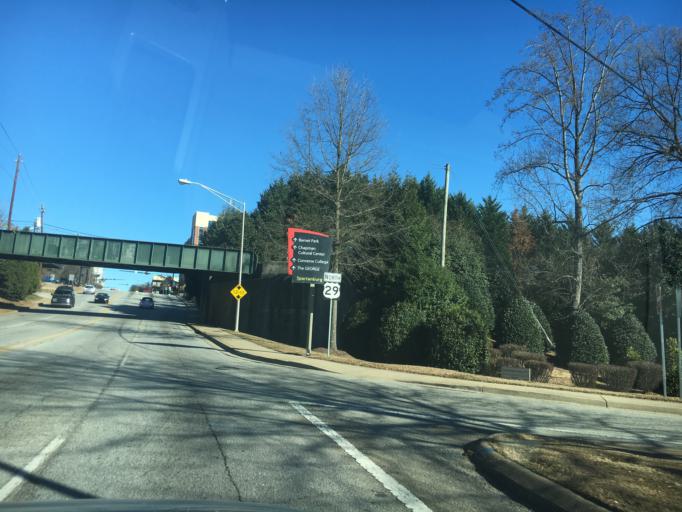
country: US
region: South Carolina
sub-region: Spartanburg County
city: Spartanburg
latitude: 34.9495
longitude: -81.9376
